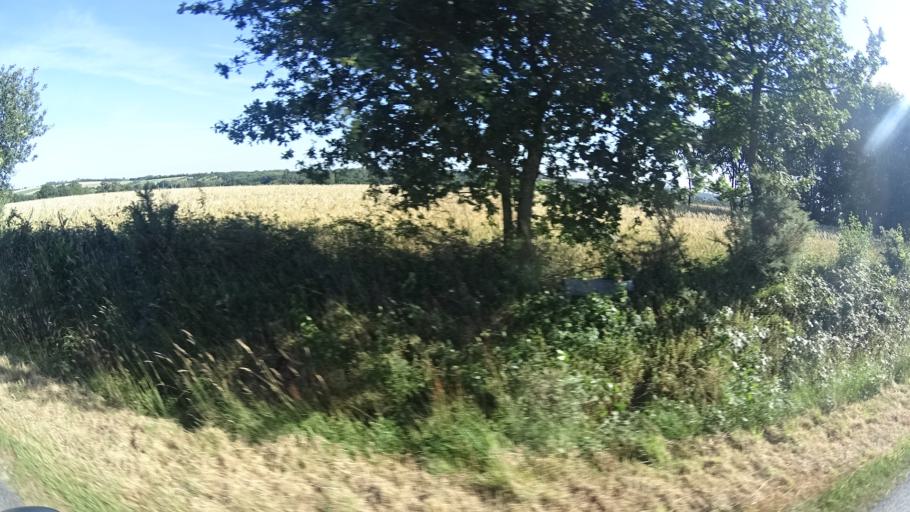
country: FR
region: Brittany
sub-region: Departement d'Ille-et-Vilaine
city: Langon
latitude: 47.7402
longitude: -1.8003
